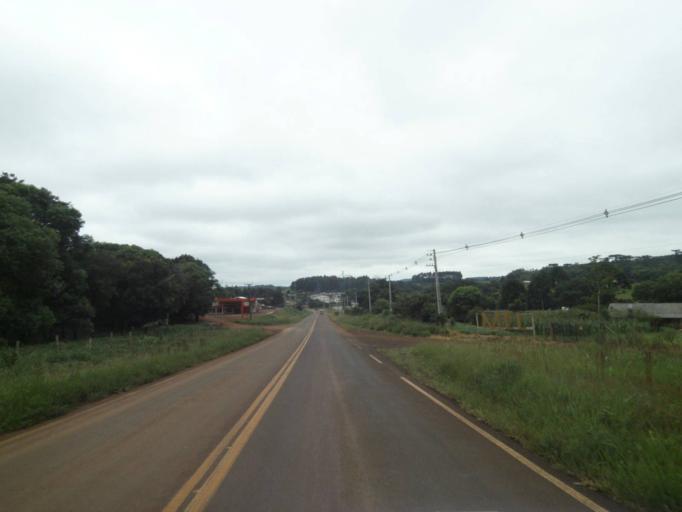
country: BR
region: Parana
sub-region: Pitanga
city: Pitanga
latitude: -24.9236
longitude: -51.8715
